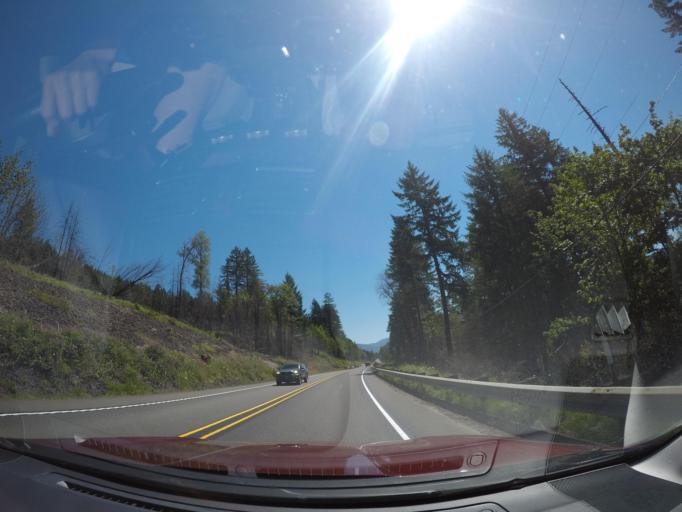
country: US
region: Oregon
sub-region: Linn County
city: Mill City
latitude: 44.7562
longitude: -122.4611
